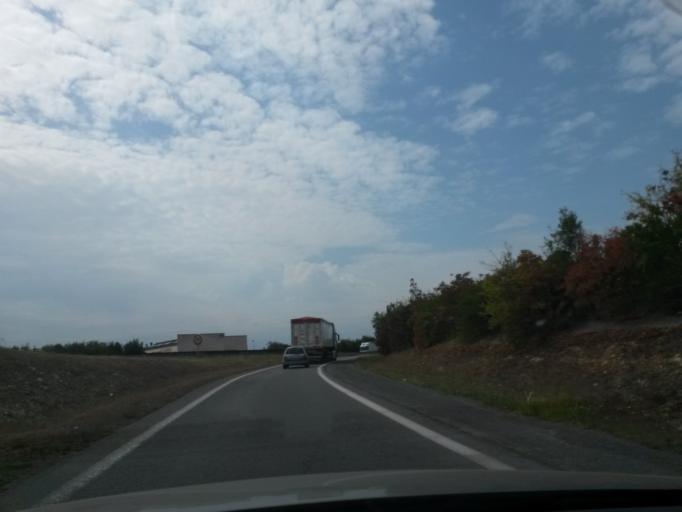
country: FR
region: Poitou-Charentes
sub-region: Departement de la Charente-Maritime
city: Saint-Xandre
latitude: 46.1810
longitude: -1.0918
